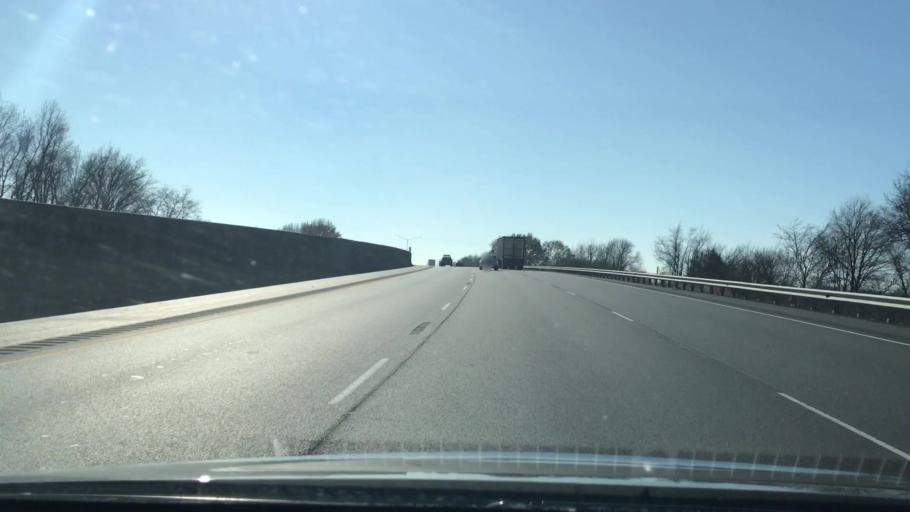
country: US
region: Kentucky
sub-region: Edmonson County
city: Brownsville
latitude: 37.0312
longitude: -86.2375
